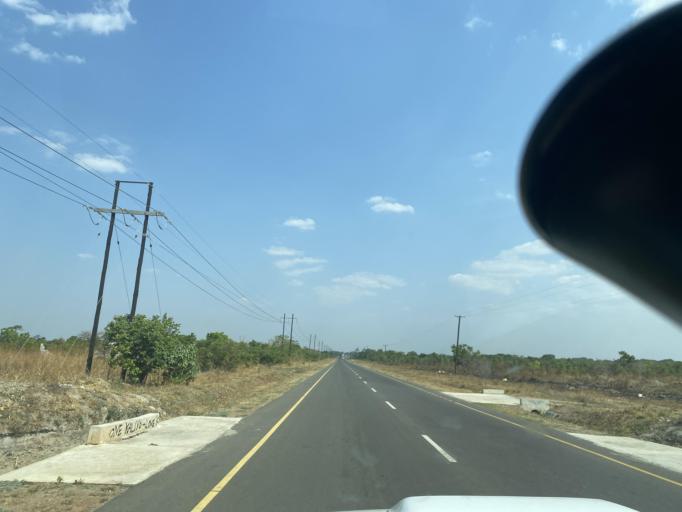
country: ZM
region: Lusaka
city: Lusaka
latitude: -15.3244
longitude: 28.0657
